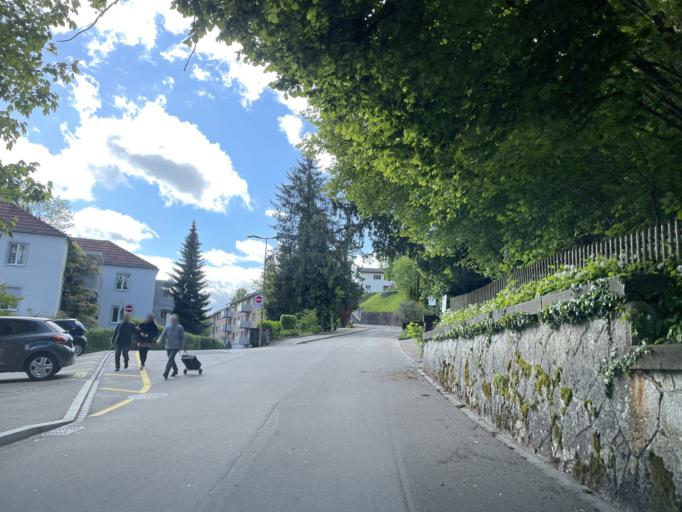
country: CH
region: Zurich
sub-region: Bezirk Winterthur
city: Stadt Winterthur (Kreis 1) / Altstadt
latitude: 47.4960
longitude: 8.7283
